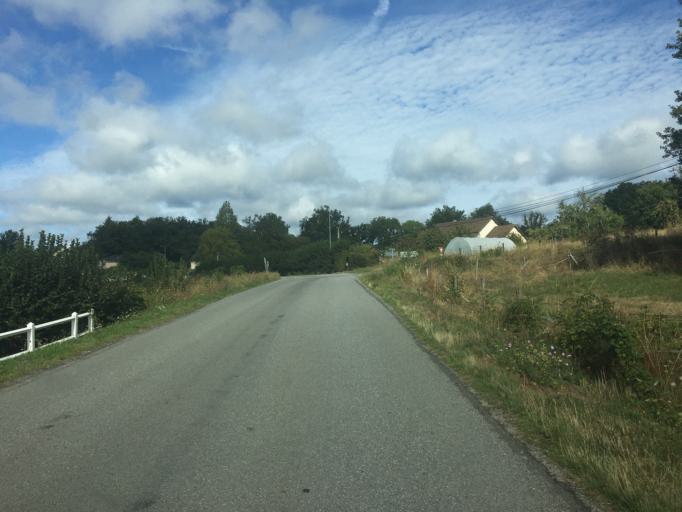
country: FR
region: Auvergne
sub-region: Departement du Cantal
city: Champagnac
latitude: 45.4143
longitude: 2.4280
